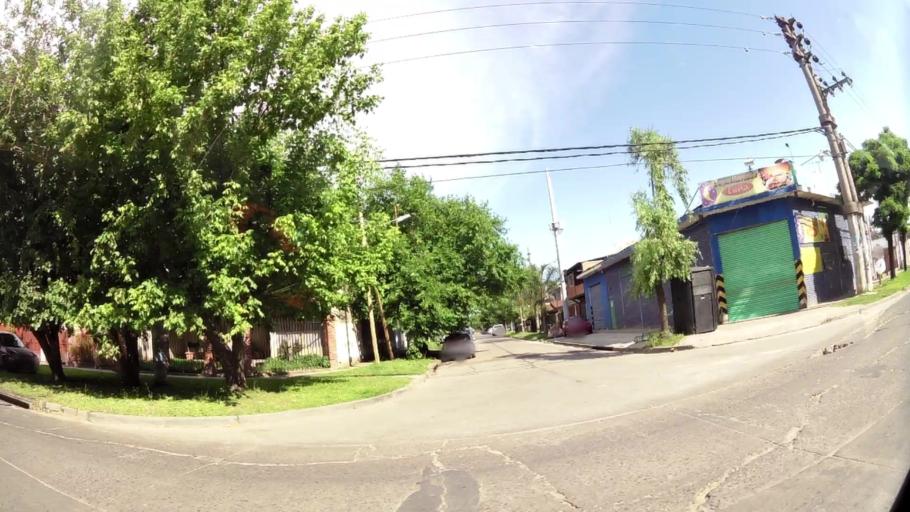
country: AR
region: Buenos Aires
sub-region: Partido de Merlo
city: Merlo
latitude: -34.6393
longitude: -58.7153
